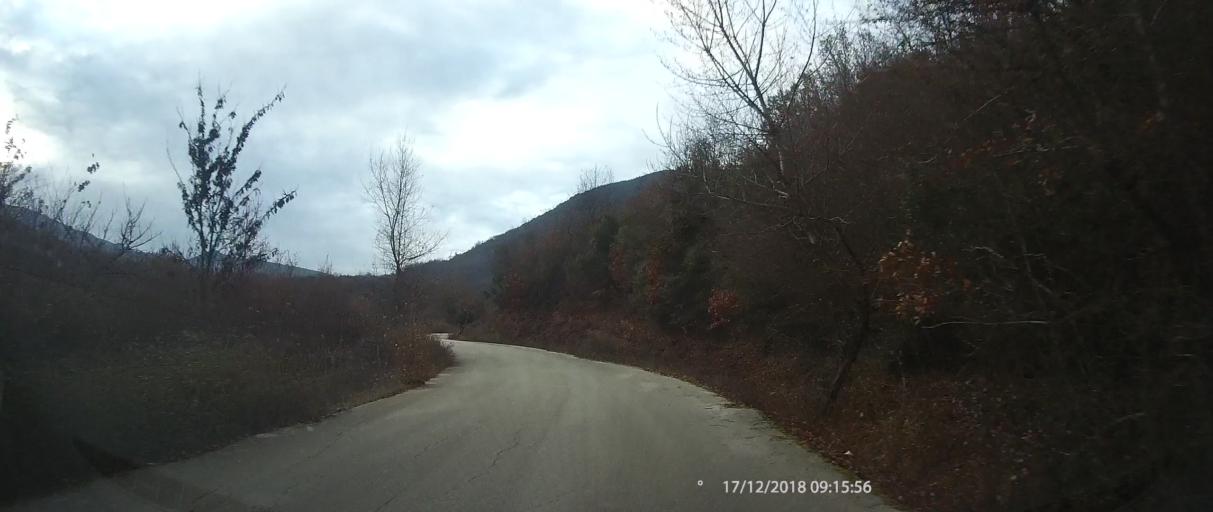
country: GR
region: Epirus
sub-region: Nomos Ioanninon
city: Kalpaki
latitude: 39.9645
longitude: 20.6568
